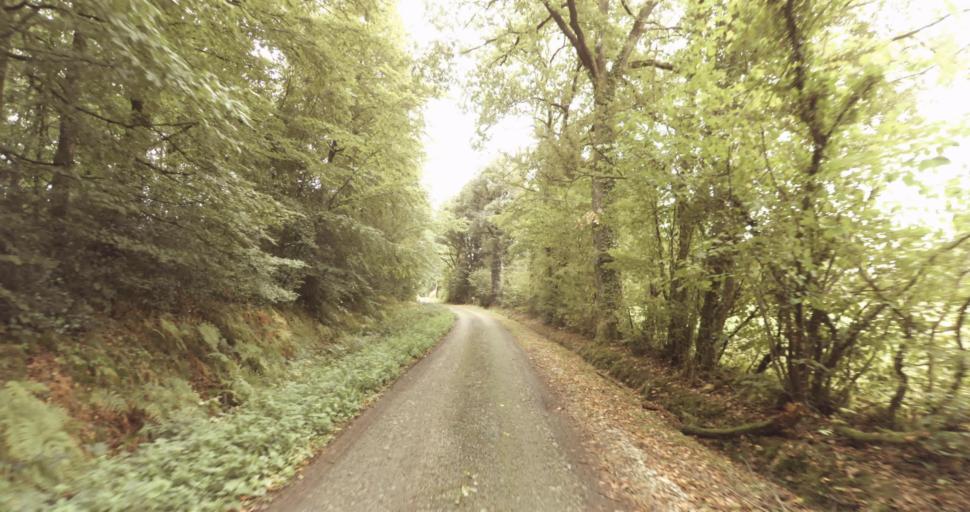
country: FR
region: Lower Normandy
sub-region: Departement de l'Orne
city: Sainte-Gauburge-Sainte-Colombe
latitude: 48.6975
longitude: 0.4559
